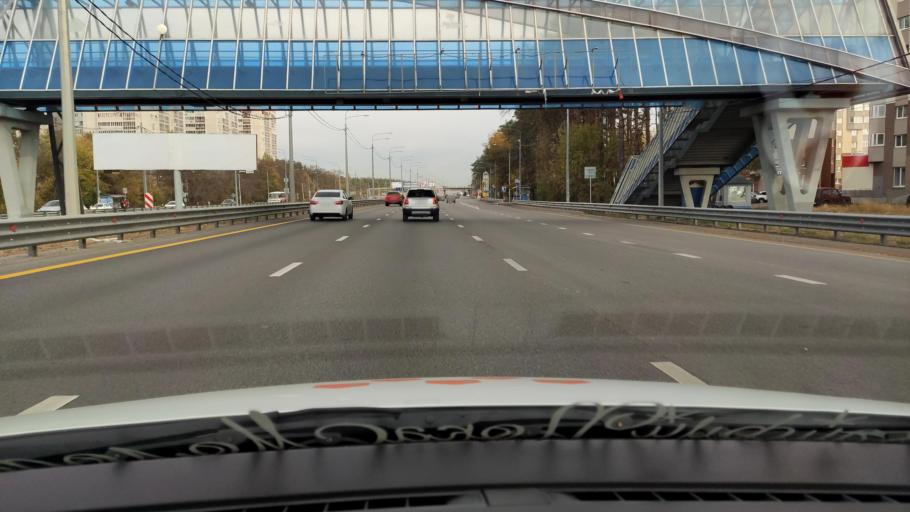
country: RU
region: Voronezj
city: Podgornoye
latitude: 51.7303
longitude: 39.1806
